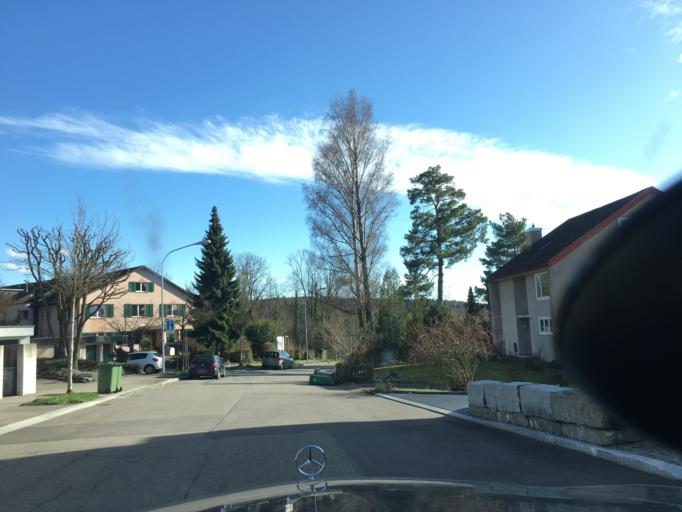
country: CH
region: Zurich
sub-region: Bezirk Zuerich
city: Zuerich (Kreis 7) / Witikon
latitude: 47.3555
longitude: 8.5846
